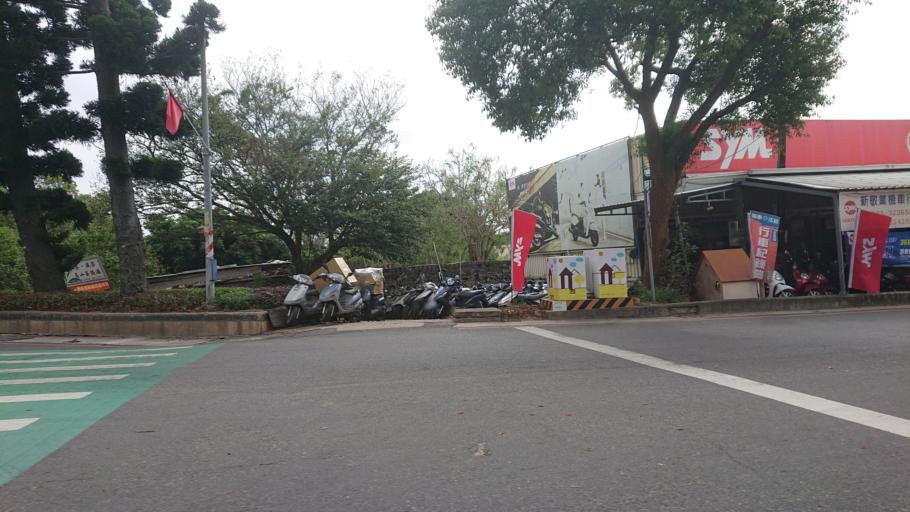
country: TW
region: Fukien
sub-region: Kinmen
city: Jincheng
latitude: 24.4313
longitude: 118.3213
